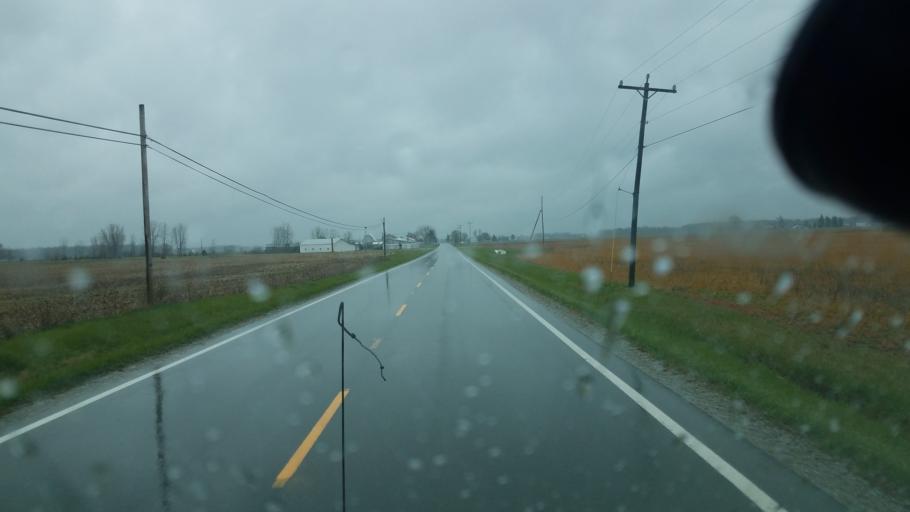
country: US
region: Ohio
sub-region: Hardin County
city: Kenton
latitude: 40.6788
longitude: -83.5189
